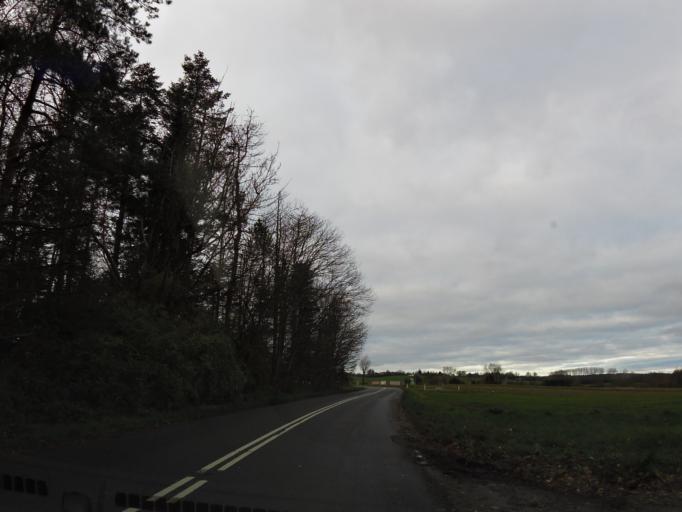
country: DK
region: Central Jutland
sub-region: Arhus Kommune
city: Beder
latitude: 56.0289
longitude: 10.2588
